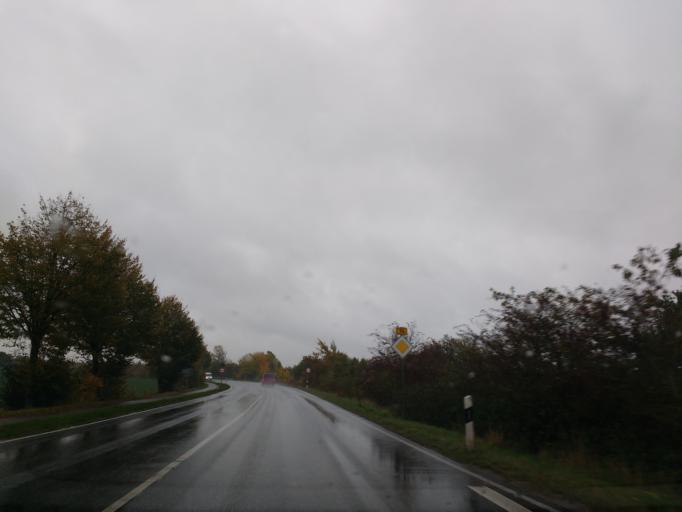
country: DE
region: Schleswig-Holstein
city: Eutin
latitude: 54.1179
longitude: 10.6435
